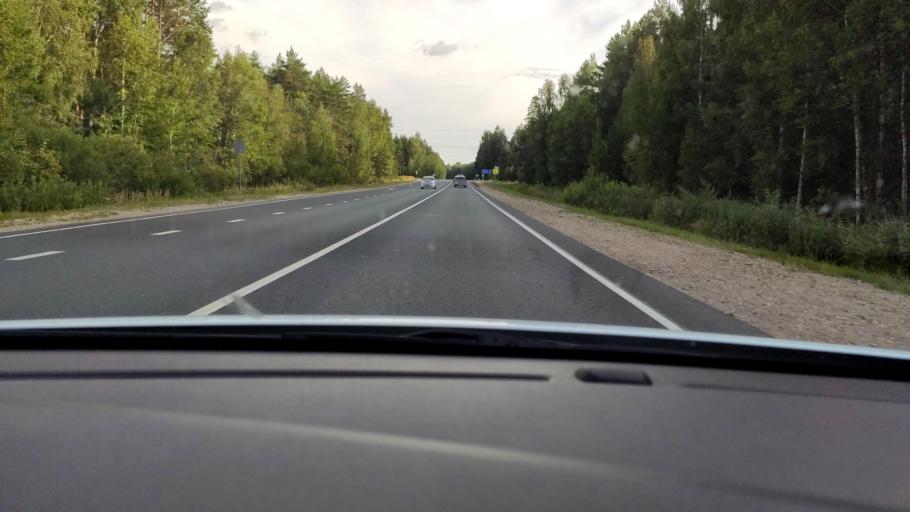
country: RU
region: Mariy-El
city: Suslonger
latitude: 56.2442
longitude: 48.2320
